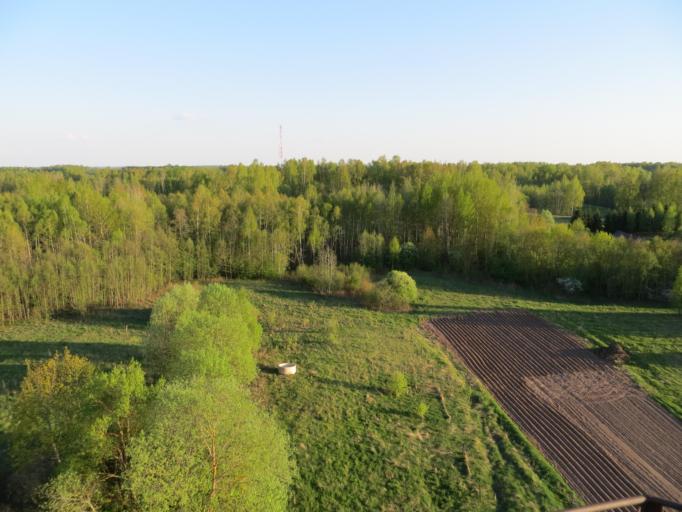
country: LT
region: Utenos apskritis
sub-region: Utena
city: Utena
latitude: 55.4177
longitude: 25.5234
